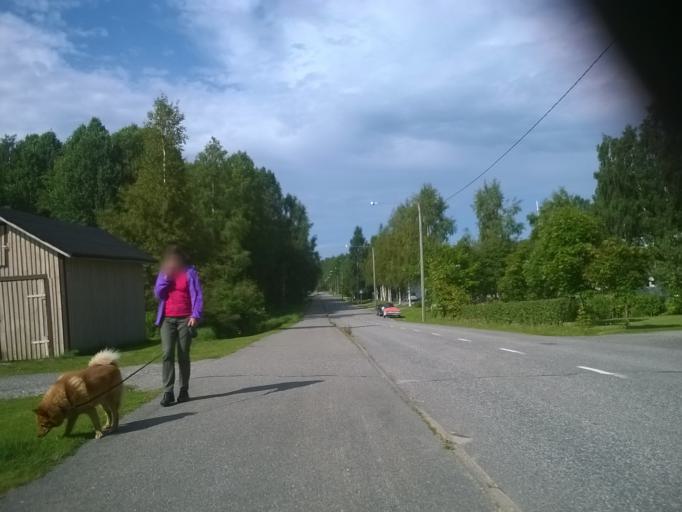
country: FI
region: Kainuu
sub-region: Kehys-Kainuu
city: Kuhmo
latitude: 64.1281
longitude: 29.5304
